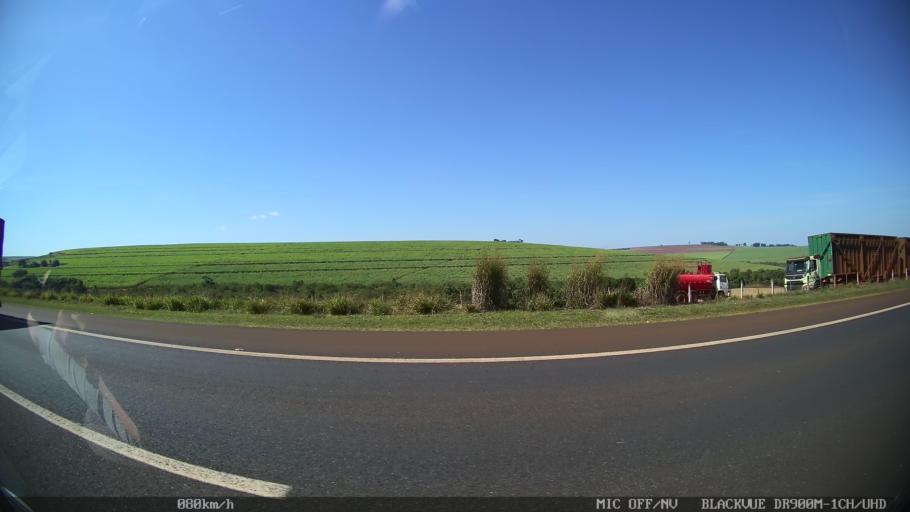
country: BR
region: Sao Paulo
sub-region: Batatais
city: Batatais
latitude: -20.7092
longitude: -47.5042
